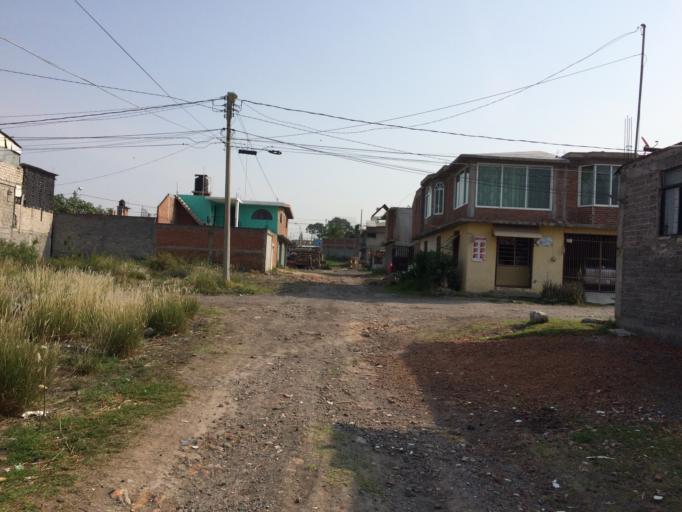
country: MX
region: Michoacan
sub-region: Tarimbaro
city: Real Hacienda (Metropolis)
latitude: 19.7237
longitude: -101.2146
